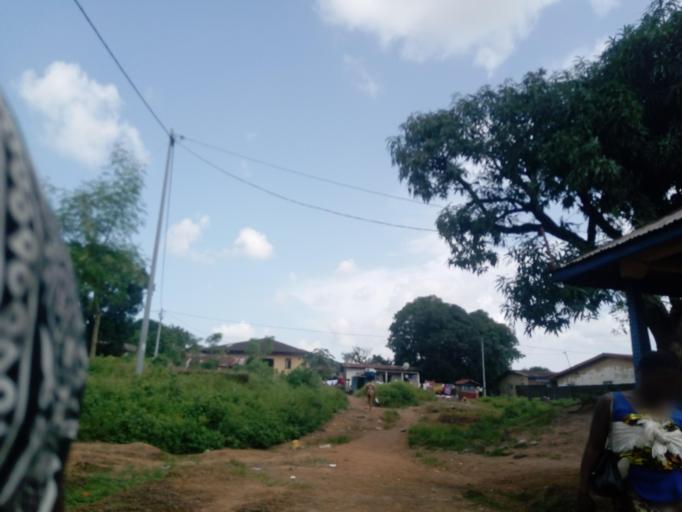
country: SL
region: Northern Province
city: Makeni
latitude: 8.8967
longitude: -12.0431
